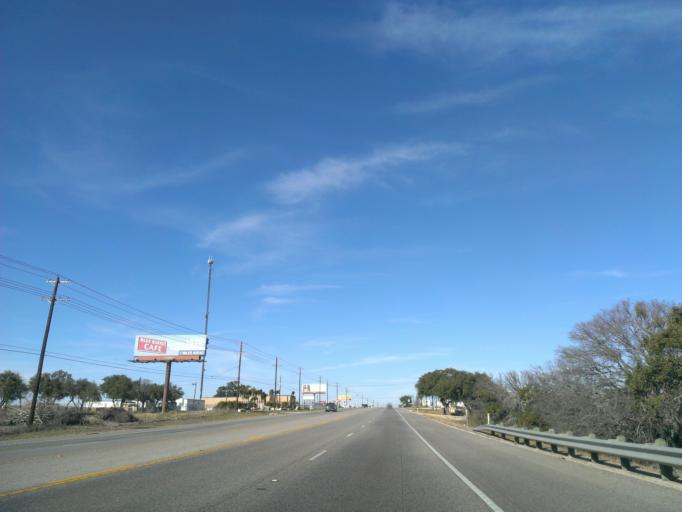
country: US
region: Texas
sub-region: Burnet County
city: Meadowlakes
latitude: 30.5431
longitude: -98.2774
